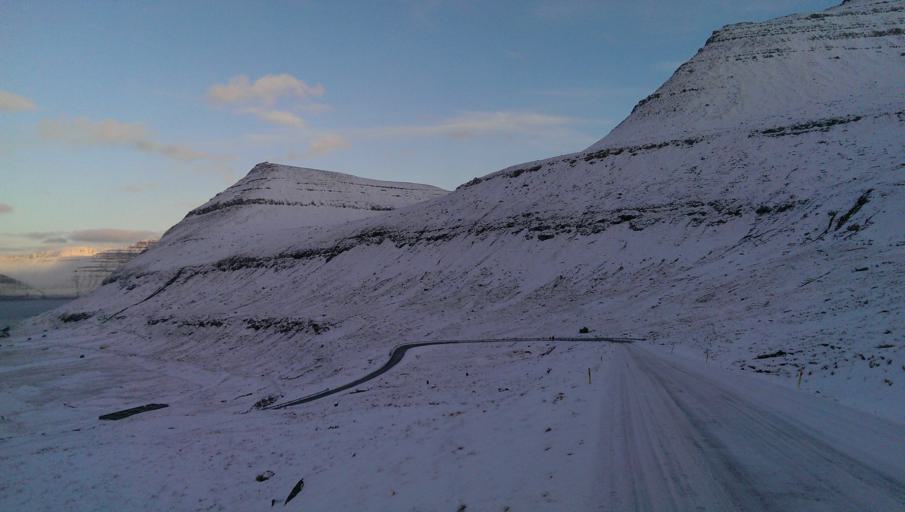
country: FO
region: Eysturoy
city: Fuglafjordur
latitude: 62.2544
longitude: -6.8647
